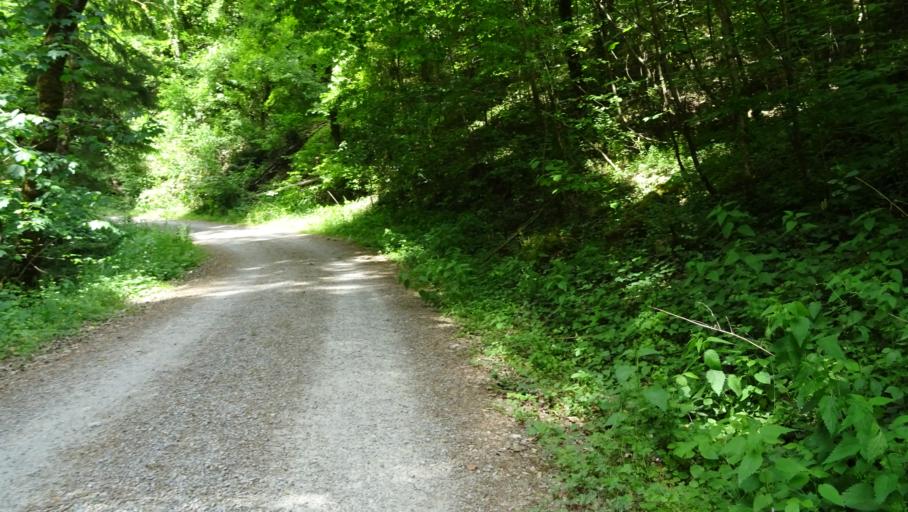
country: DE
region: Baden-Wuerttemberg
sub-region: Karlsruhe Region
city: Hassmersheim
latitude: 49.2953
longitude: 9.1600
